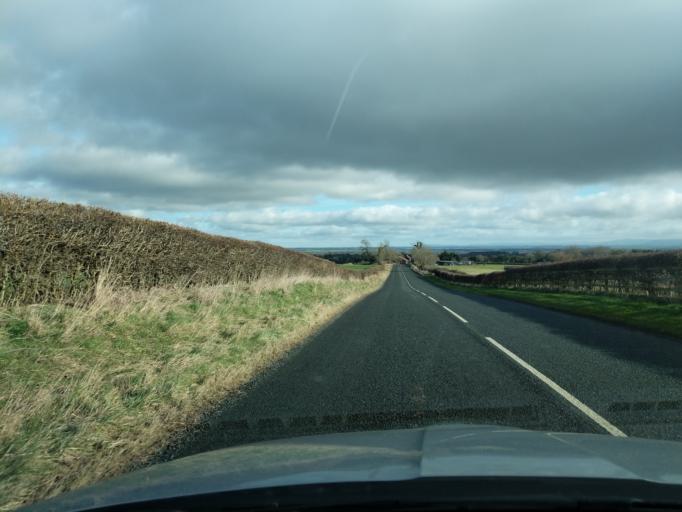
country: GB
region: England
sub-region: North Yorkshire
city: Catterick Garrison
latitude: 54.3526
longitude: -1.6806
